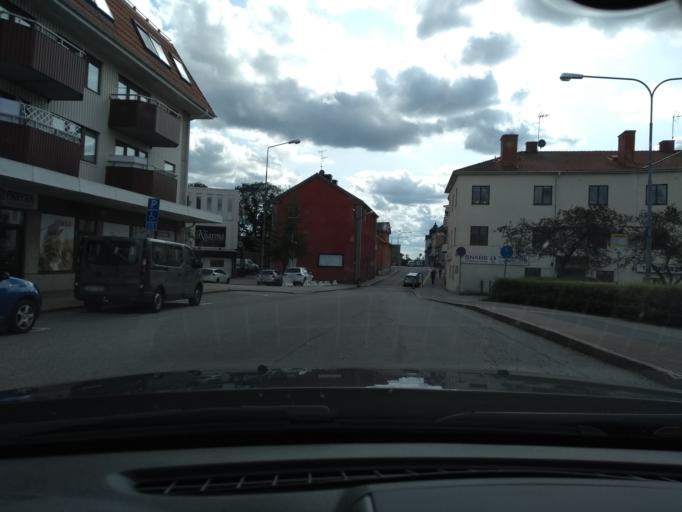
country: SE
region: Kalmar
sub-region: Vimmerby Kommun
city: Vimmerby
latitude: 57.6669
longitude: 15.8569
